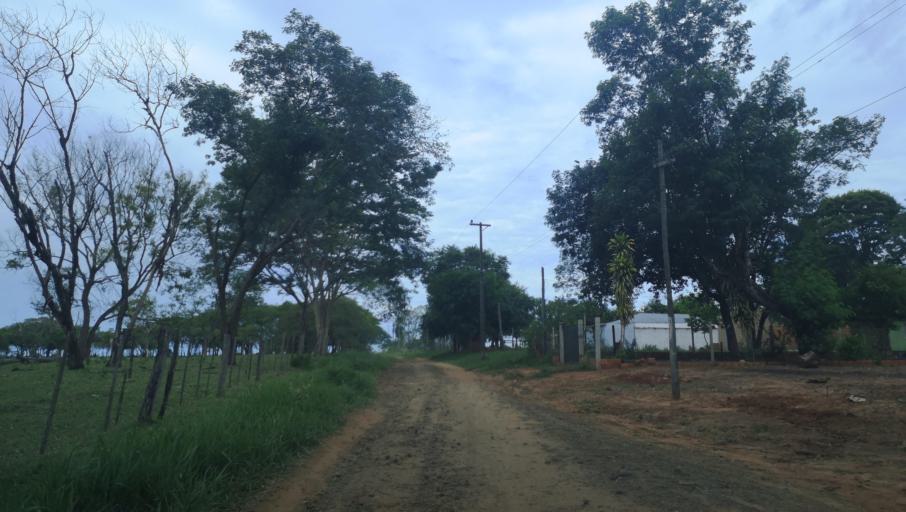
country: PY
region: San Pedro
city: Capiibary
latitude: -24.7389
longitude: -56.0180
